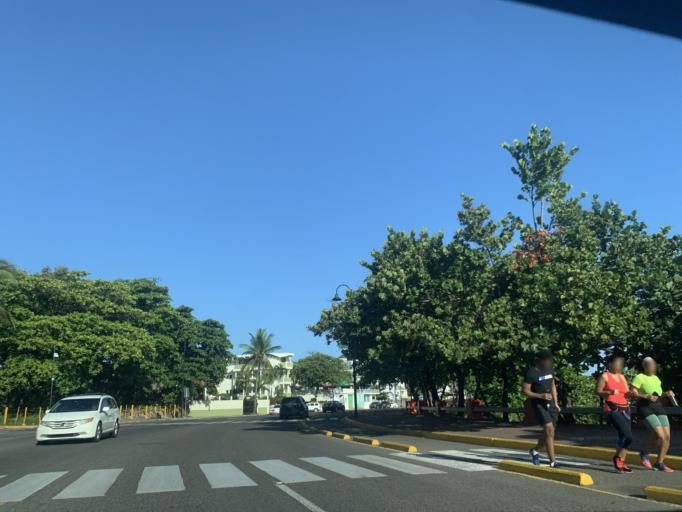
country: DO
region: Puerto Plata
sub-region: Puerto Plata
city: Puerto Plata
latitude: 19.7927
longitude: -70.6773
